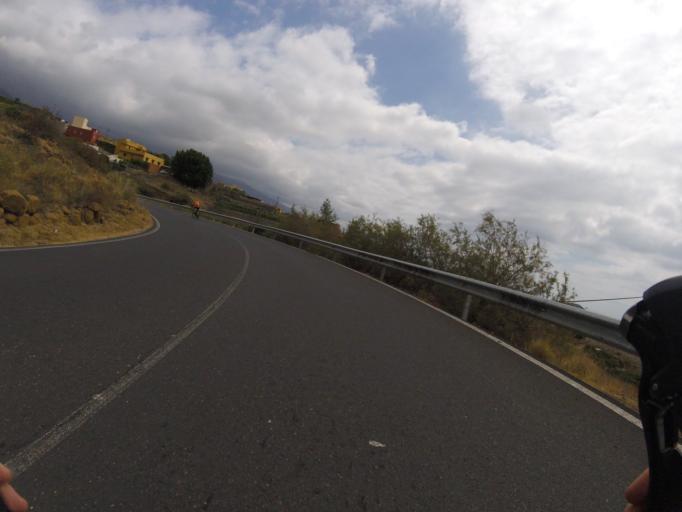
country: ES
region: Canary Islands
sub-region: Provincia de Santa Cruz de Tenerife
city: Guimar
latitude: 28.3059
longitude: -16.4146
